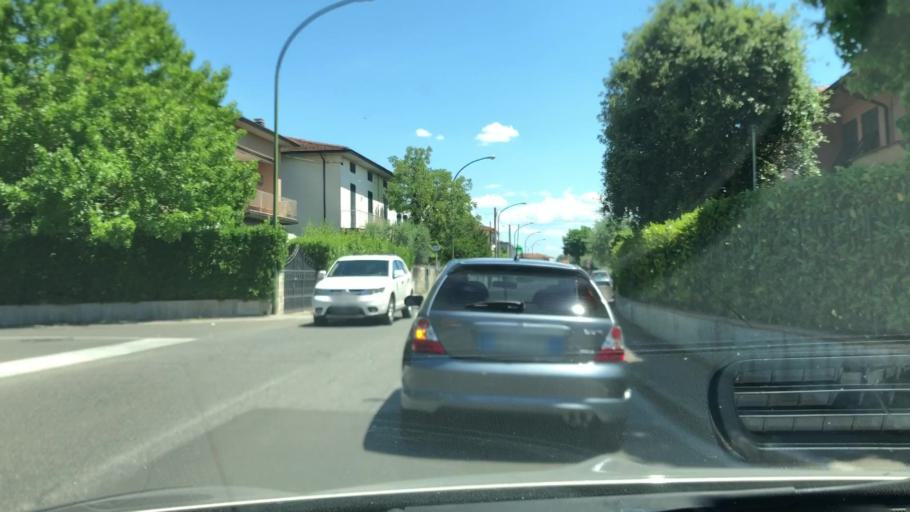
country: IT
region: Tuscany
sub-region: Province of Pisa
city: Ponsacco
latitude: 43.6176
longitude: 10.6377
